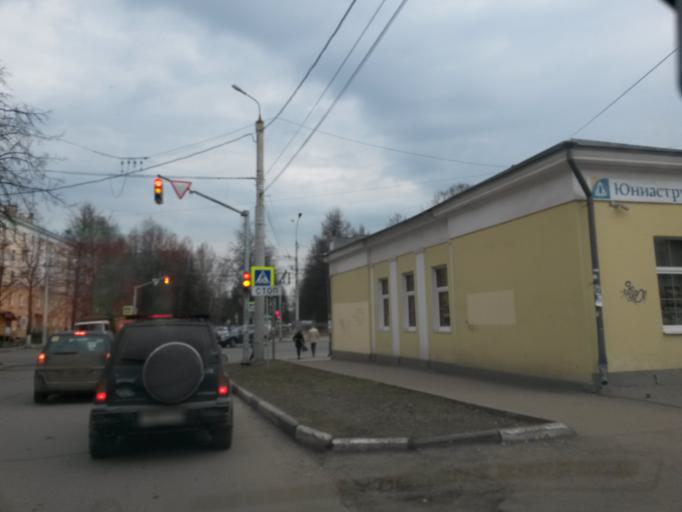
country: RU
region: Jaroslavl
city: Yaroslavl
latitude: 57.6260
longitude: 39.8625
